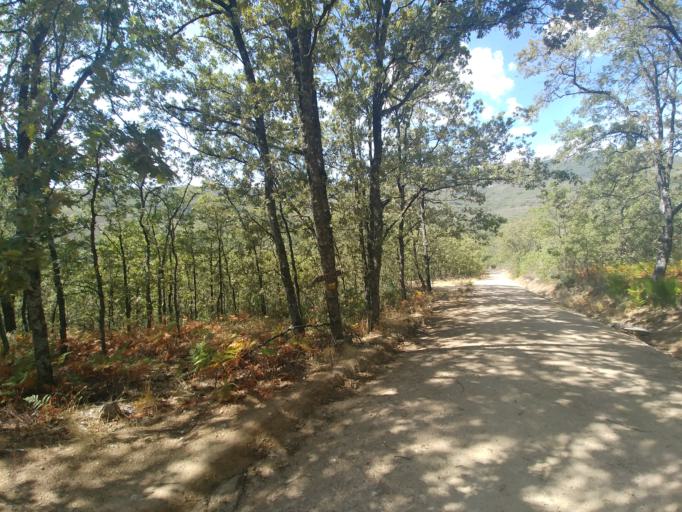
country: ES
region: Extremadura
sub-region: Provincia de Caceres
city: Garganta la Olla
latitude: 40.1021
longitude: -5.7388
